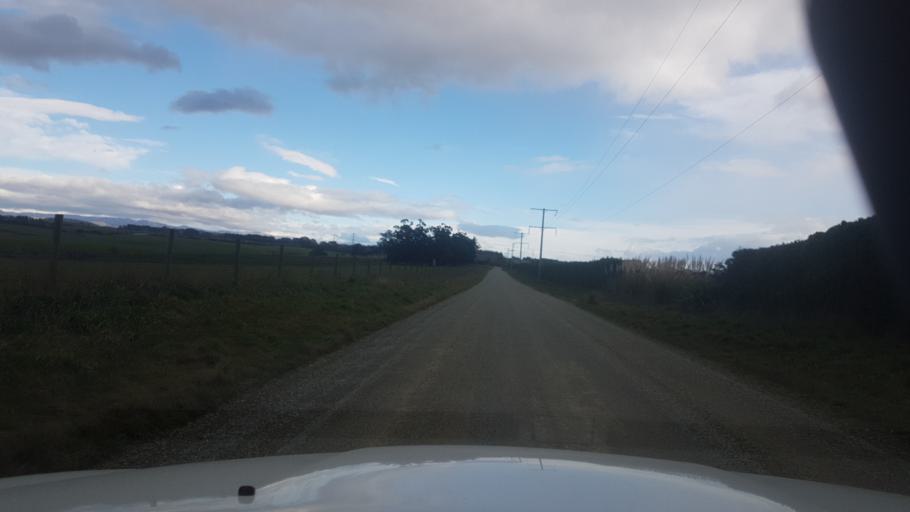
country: NZ
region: Canterbury
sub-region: Timaru District
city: Pleasant Point
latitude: -44.3549
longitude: 171.1372
